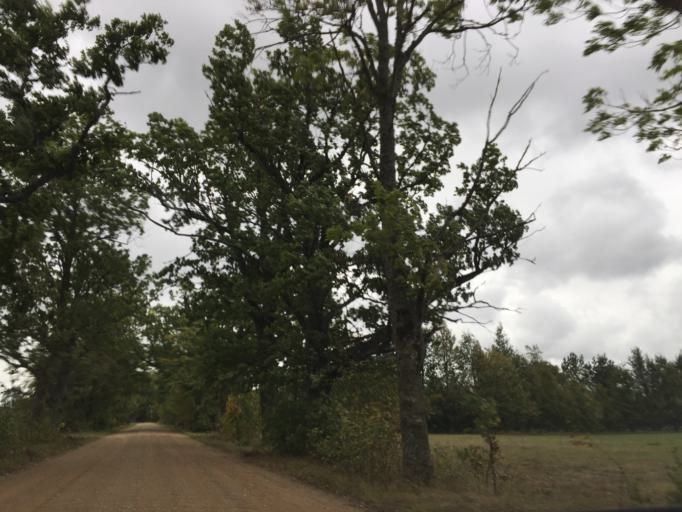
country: LV
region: Salacgrivas
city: Salacgriva
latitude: 57.6733
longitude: 24.3763
